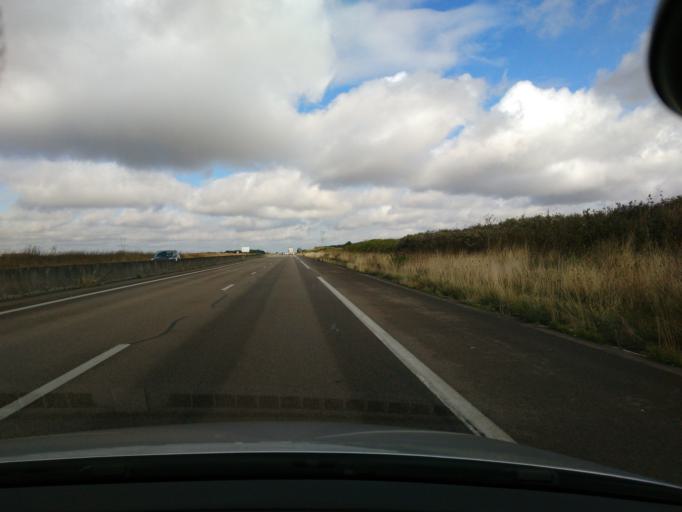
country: FR
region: Haute-Normandie
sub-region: Departement de l'Eure
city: La Madeleine-de-Nonancourt
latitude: 48.8440
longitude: 1.1814
